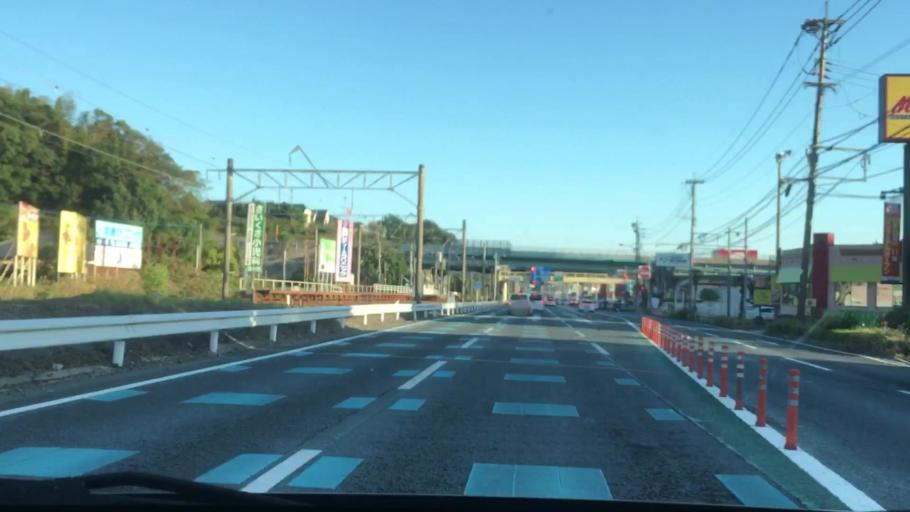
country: JP
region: Nagasaki
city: Sasebo
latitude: 33.1503
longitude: 129.7808
